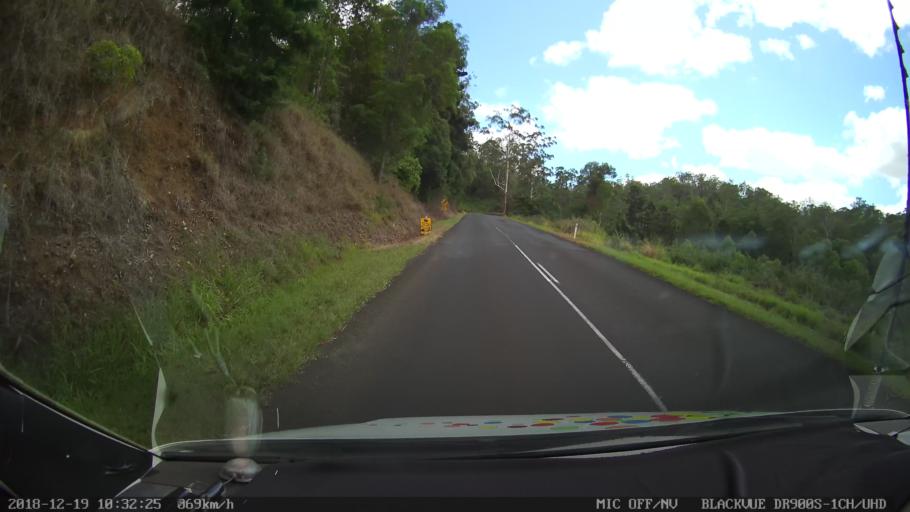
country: AU
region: New South Wales
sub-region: Lismore Municipality
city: Larnook
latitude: -28.5819
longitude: 153.1210
